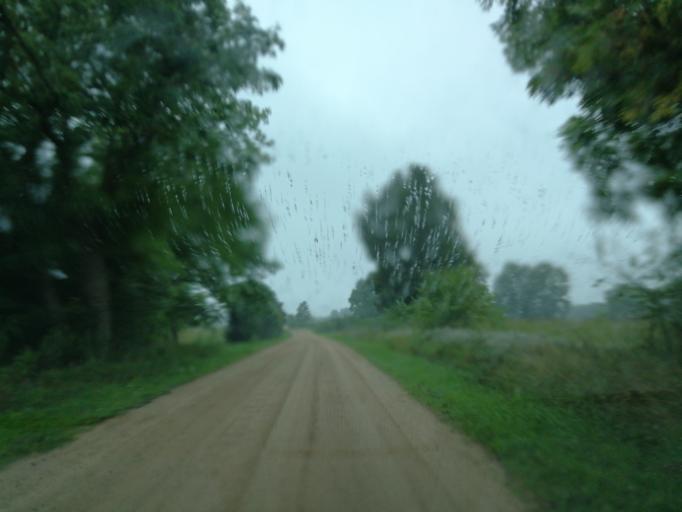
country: LV
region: Preilu Rajons
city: Jaunaglona
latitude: 56.3097
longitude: 26.9984
